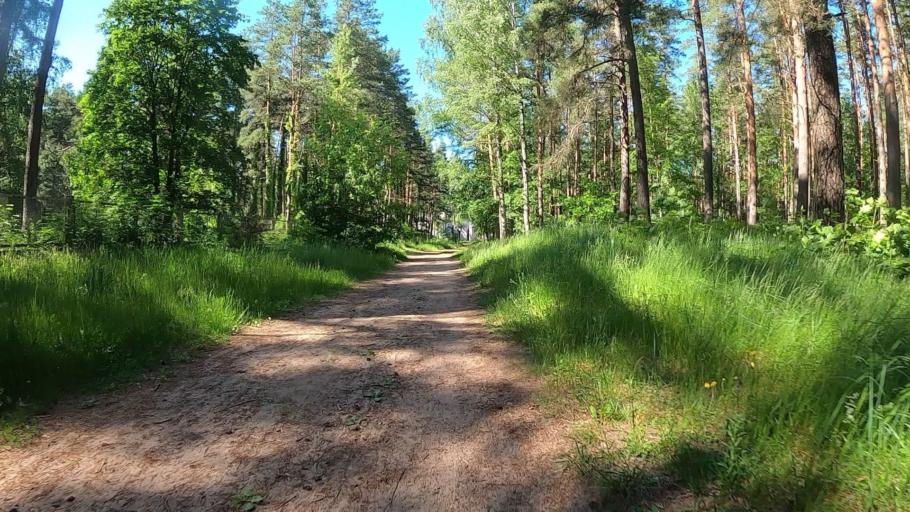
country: LV
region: Riga
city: Jaunciems
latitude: 56.9746
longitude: 24.2005
